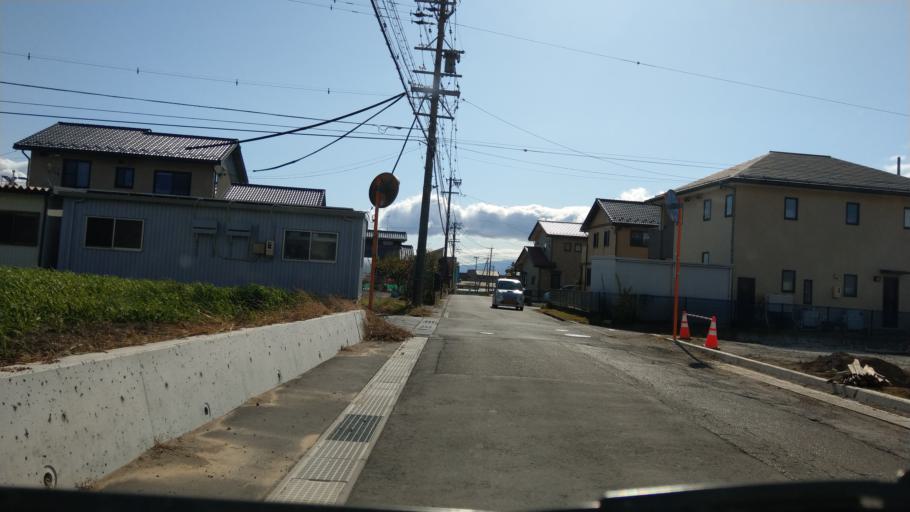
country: JP
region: Nagano
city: Komoro
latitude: 36.3079
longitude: 138.4691
